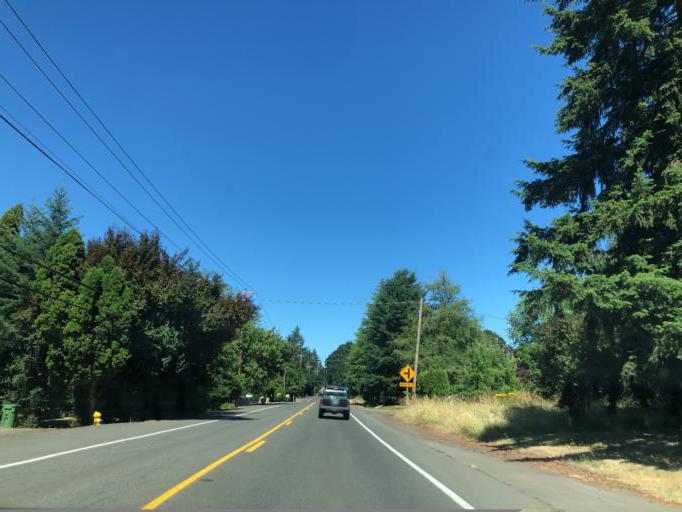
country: US
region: Oregon
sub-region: Marion County
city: Silverton
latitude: 45.0119
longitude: -122.7712
